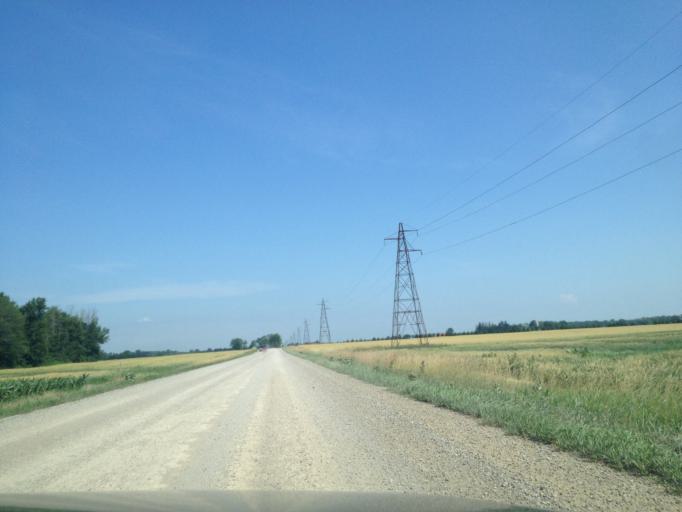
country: CA
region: Ontario
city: London
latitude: 43.1126
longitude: -81.2308
